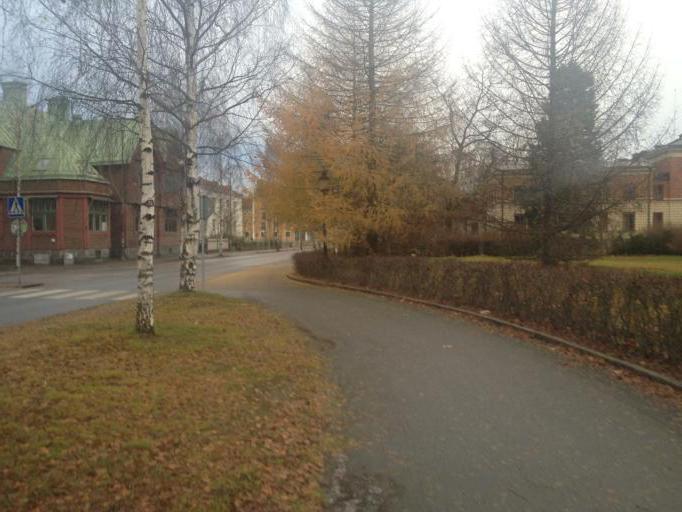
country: SE
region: Vaesterbotten
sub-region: Umea Kommun
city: Umea
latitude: 63.8234
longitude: 20.2711
